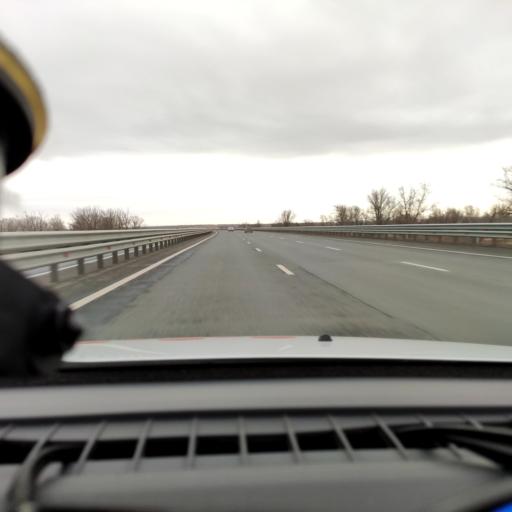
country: RU
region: Samara
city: Smyshlyayevka
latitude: 53.1703
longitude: 50.3153
